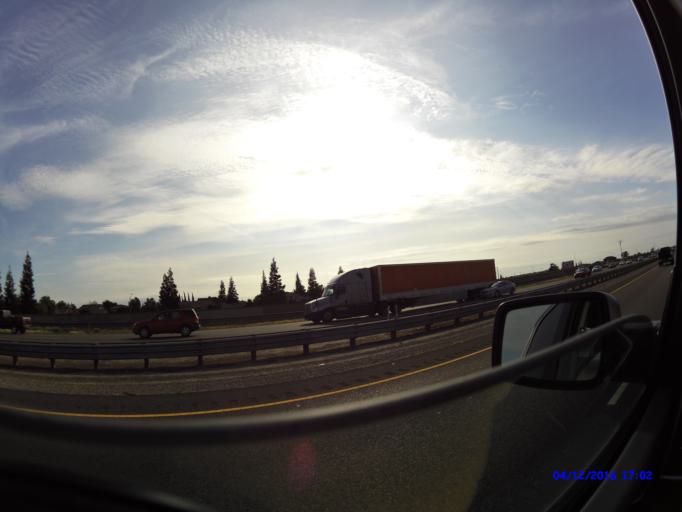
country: US
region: California
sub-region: Stanislaus County
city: Salida
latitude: 37.7166
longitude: -121.0933
